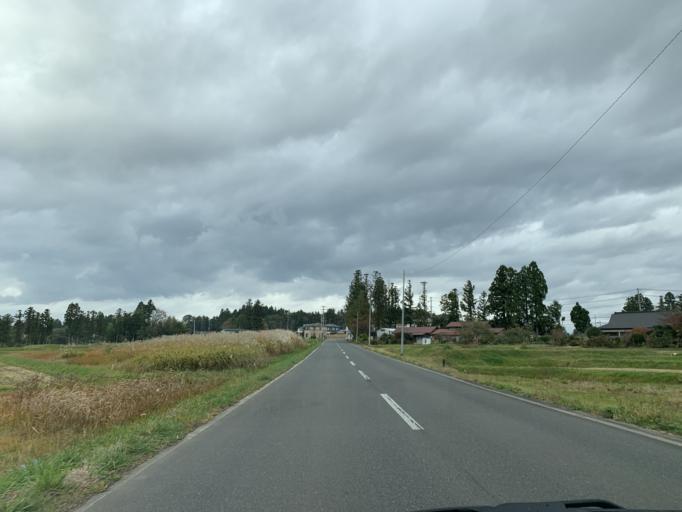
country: JP
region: Iwate
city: Mizusawa
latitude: 39.0564
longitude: 141.1110
